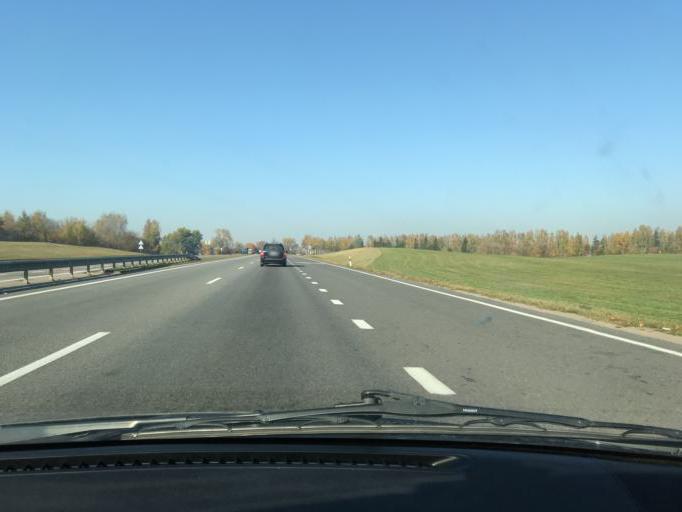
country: BY
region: Minsk
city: Samakhvalavichy
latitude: 53.7057
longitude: 27.5241
